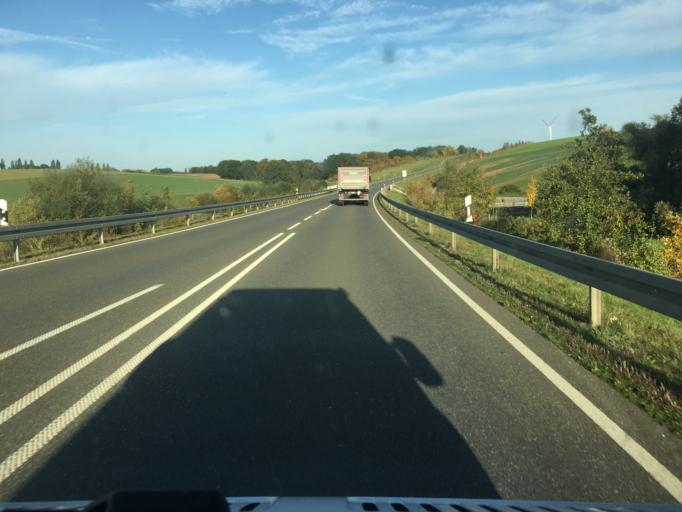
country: DE
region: Saxony
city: Neukirchen
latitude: 50.8080
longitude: 12.3539
